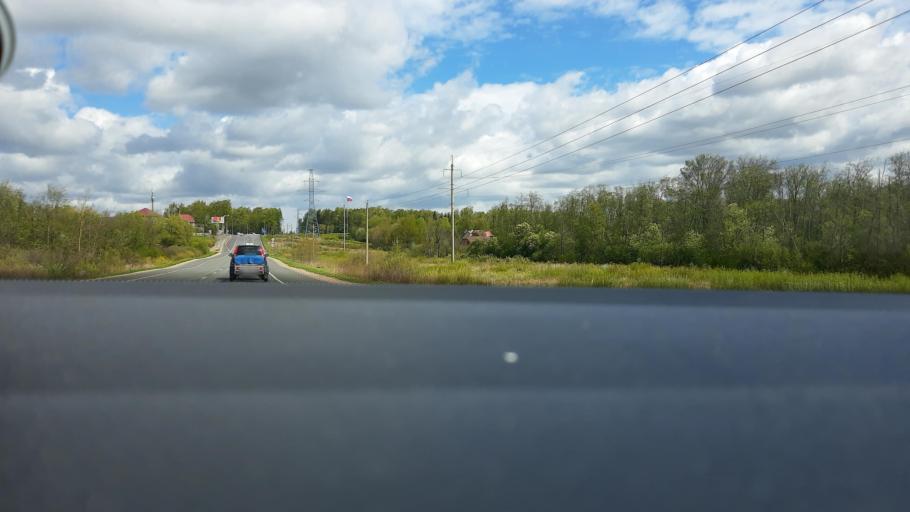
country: RU
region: Moskovskaya
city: Dmitrov
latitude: 56.3529
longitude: 37.4867
